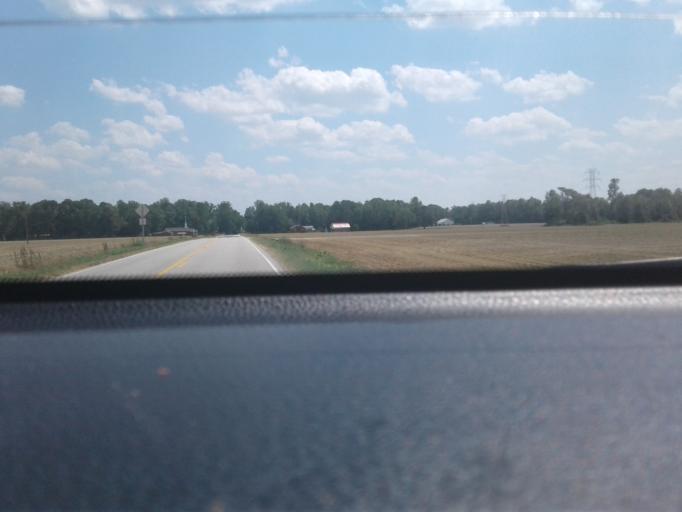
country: US
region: North Carolina
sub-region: Harnett County
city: Erwin
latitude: 35.2868
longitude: -78.6718
